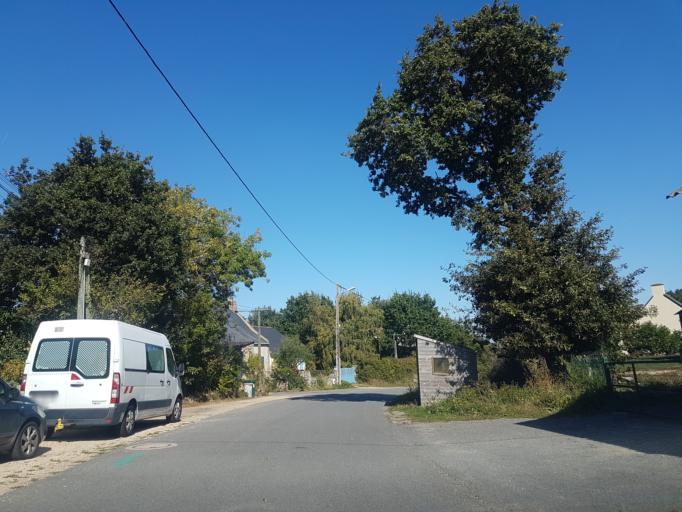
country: FR
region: Pays de la Loire
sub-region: Departement de la Loire-Atlantique
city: Mesquer
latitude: 47.3989
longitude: -2.4469
